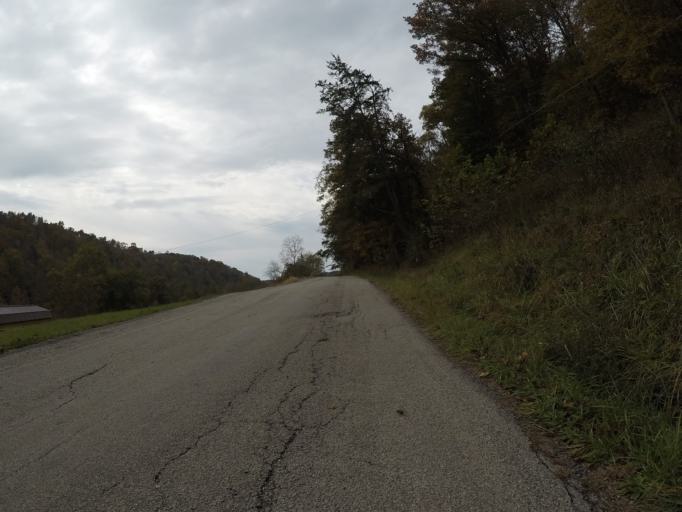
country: US
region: West Virginia
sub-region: Wayne County
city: Lavalette
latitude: 38.3471
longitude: -82.4241
